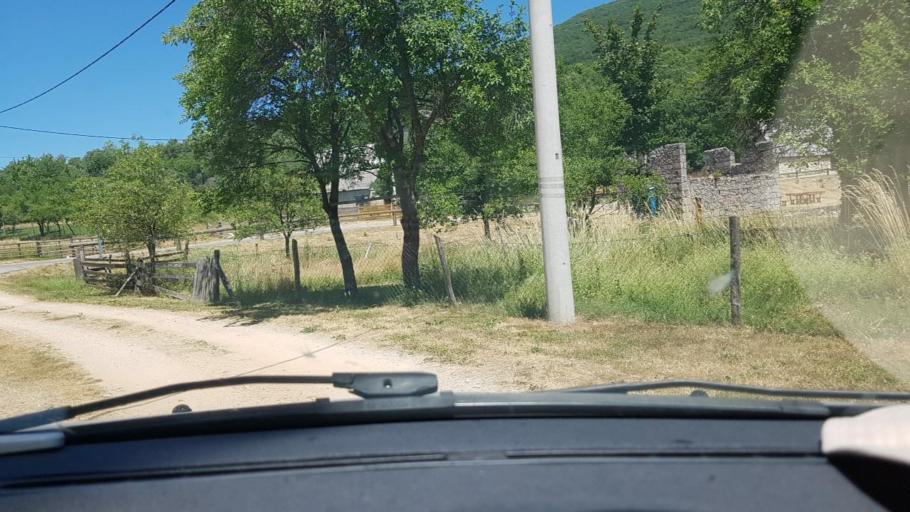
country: HR
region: Licko-Senjska
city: Otocac
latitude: 44.8144
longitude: 15.3576
